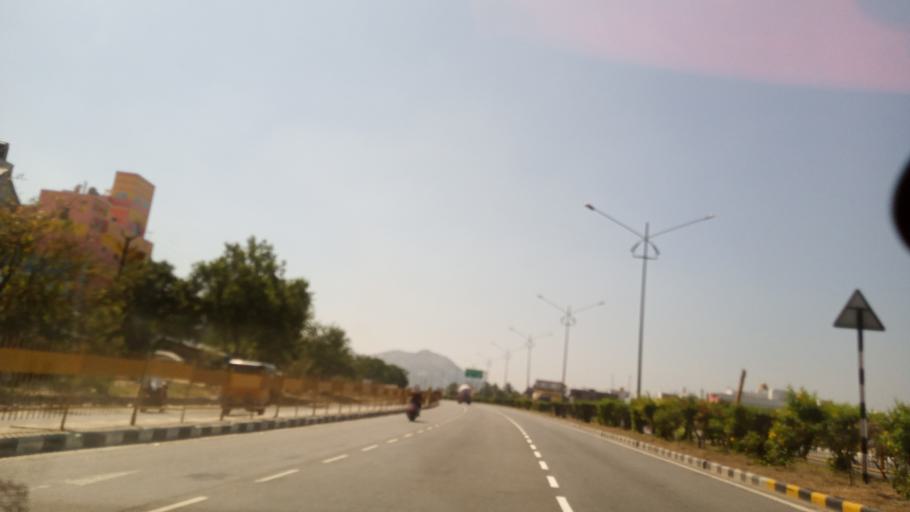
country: IN
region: Tamil Nadu
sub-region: Krishnagiri
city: Krishnagiri
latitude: 12.5225
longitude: 78.2313
